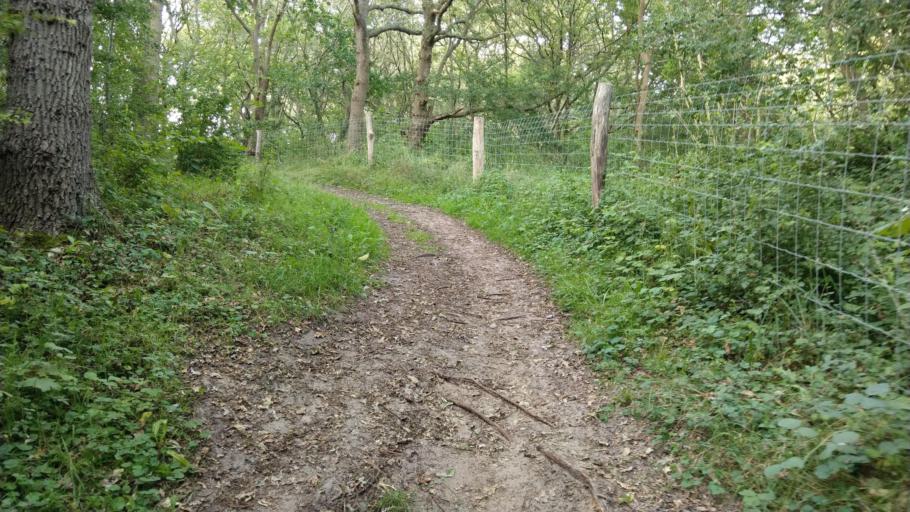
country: NL
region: North Holland
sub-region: Gemeente Castricum
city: Castricum
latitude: 52.5539
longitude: 4.6491
